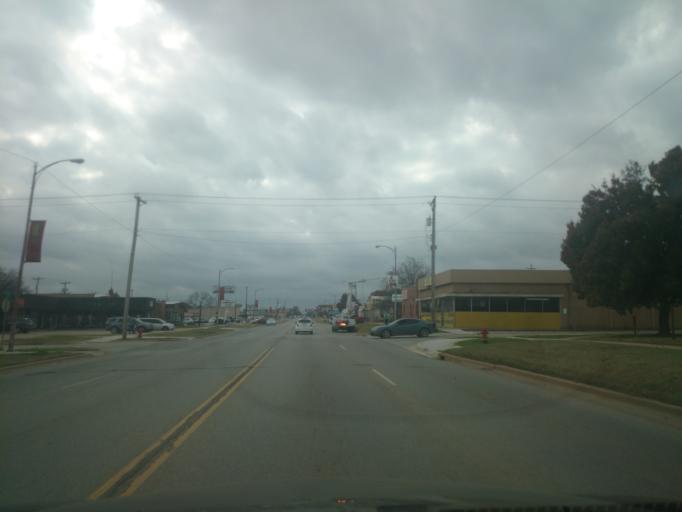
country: US
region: Oklahoma
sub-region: Payne County
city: Stillwater
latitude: 36.1210
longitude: -97.0587
